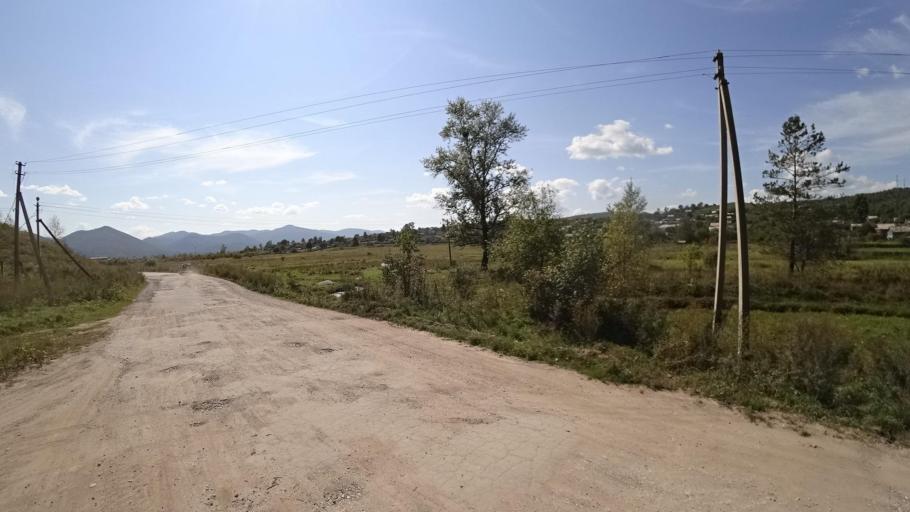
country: RU
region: Jewish Autonomous Oblast
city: Londoko
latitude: 49.0118
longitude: 131.8779
